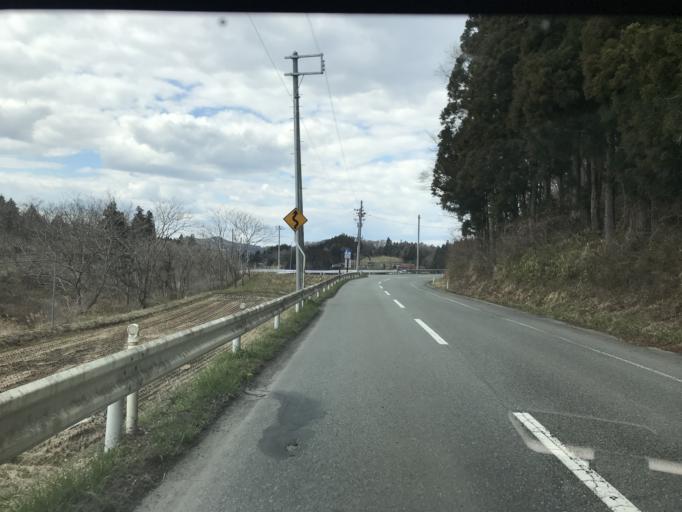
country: JP
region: Iwate
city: Ichinoseki
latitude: 38.8440
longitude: 141.3421
